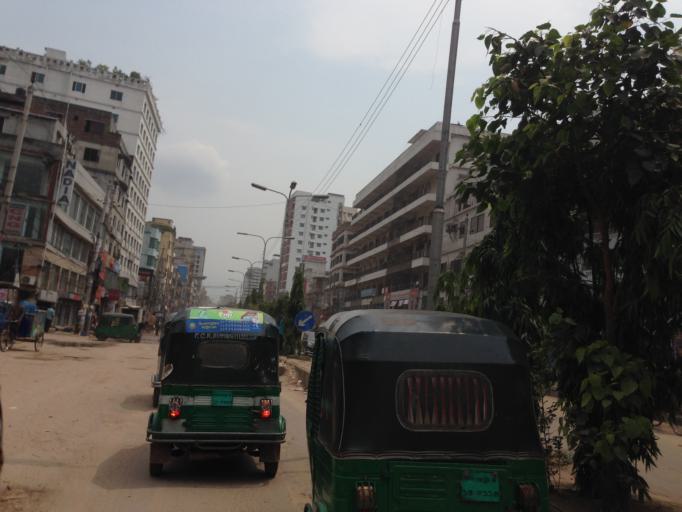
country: BD
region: Dhaka
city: Paltan
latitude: 23.7574
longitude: 90.4172
